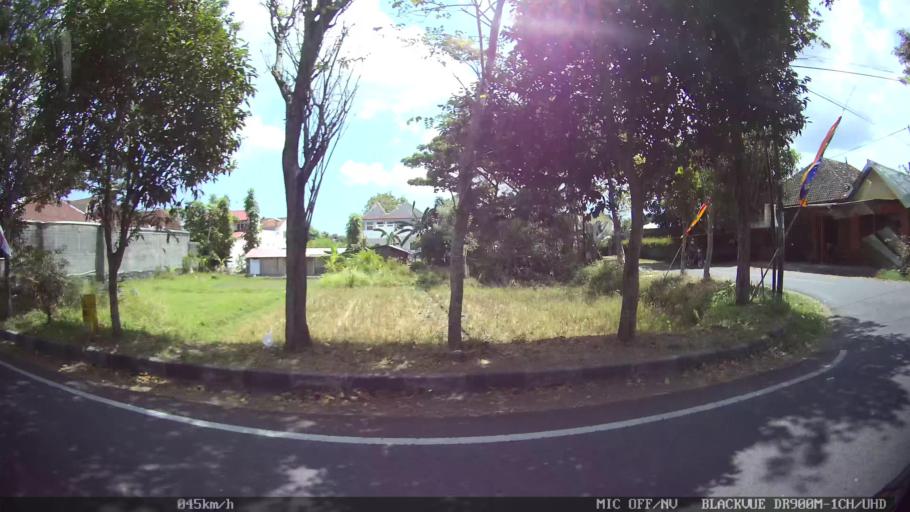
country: ID
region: Daerah Istimewa Yogyakarta
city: Bantul
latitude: -7.8828
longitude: 110.3358
